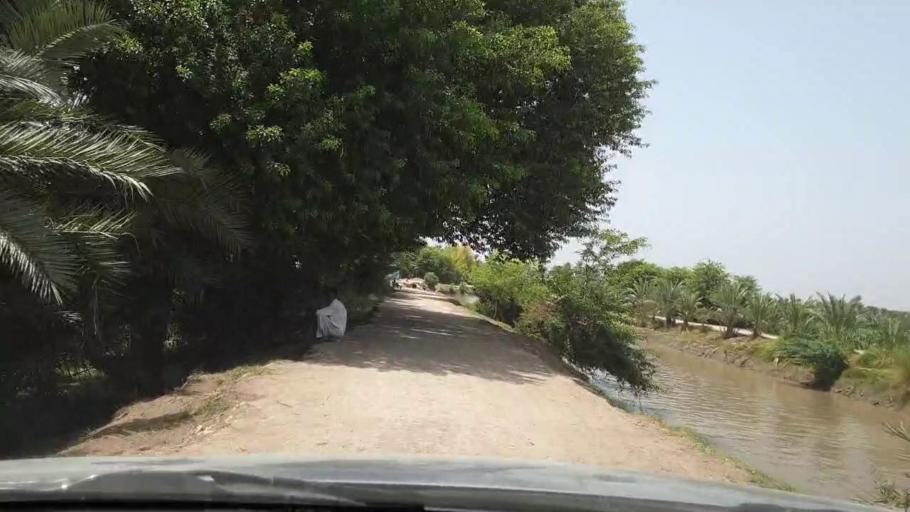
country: PK
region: Sindh
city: Pano Aqil
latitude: 27.8922
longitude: 69.1375
